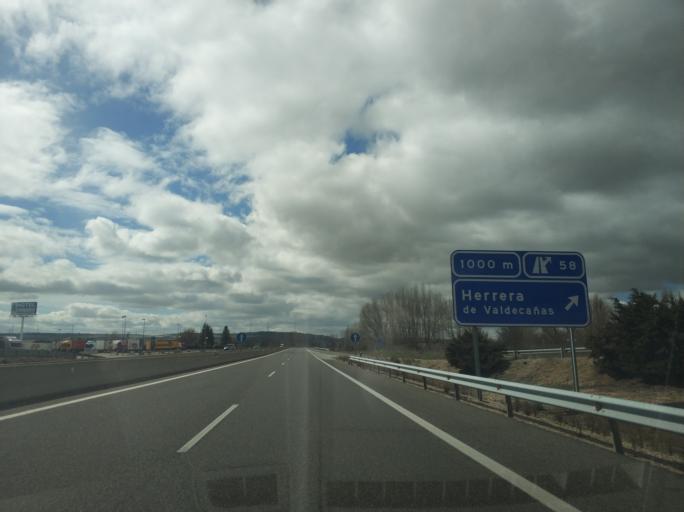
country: ES
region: Castille and Leon
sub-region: Provincia de Palencia
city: Quintana del Puente
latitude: 42.0784
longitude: -4.2111
